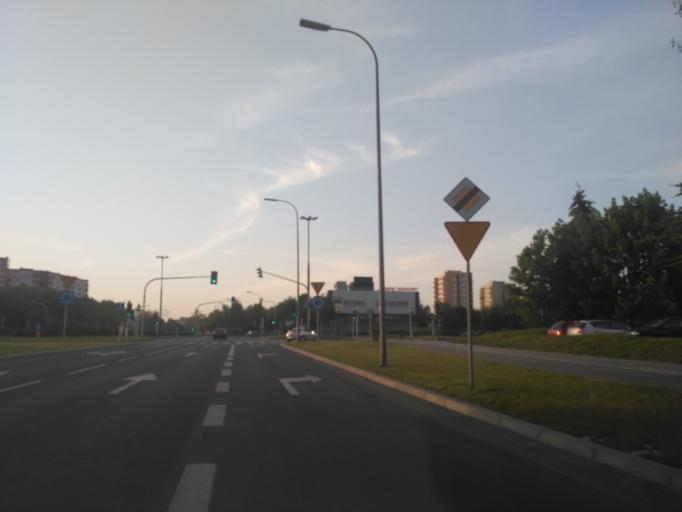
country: PL
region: Lublin Voivodeship
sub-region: Powiat lubelski
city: Lublin
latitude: 51.2617
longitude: 22.5524
